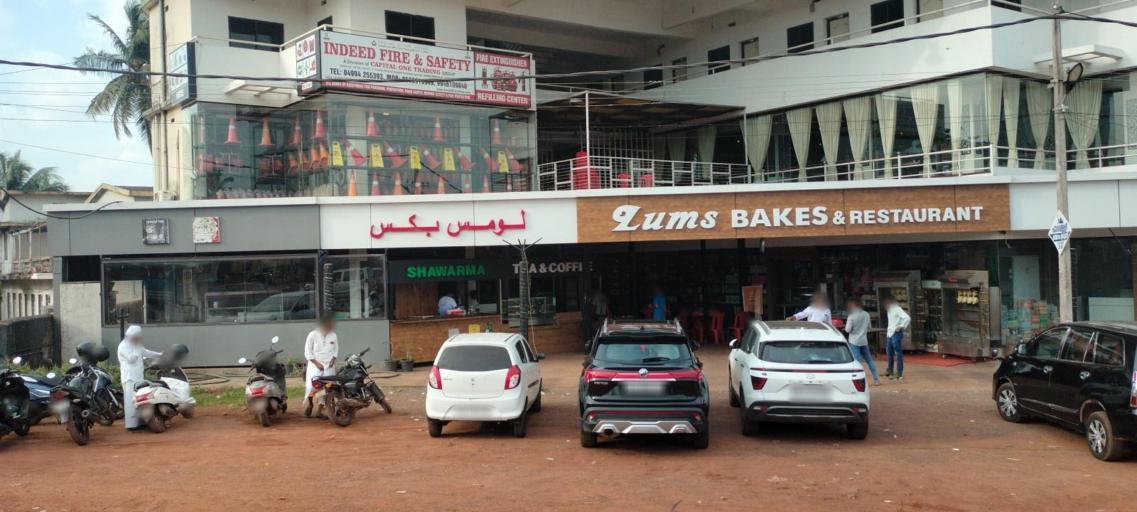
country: IN
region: Kerala
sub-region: Kasaragod District
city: Kasaragod
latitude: 12.5164
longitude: 75.0210
